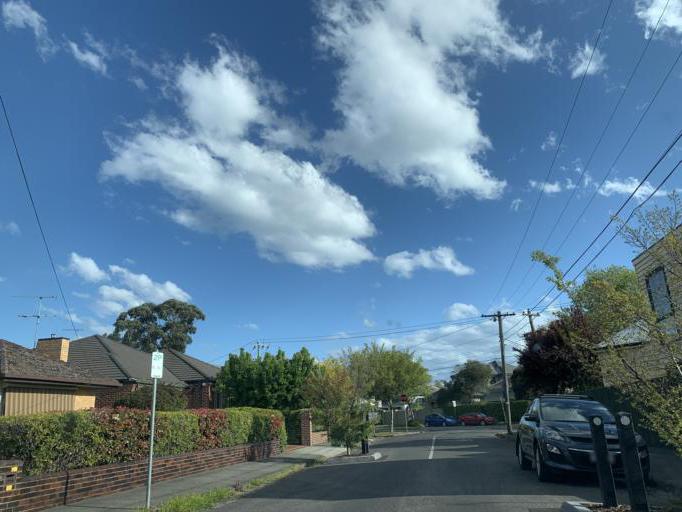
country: AU
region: Victoria
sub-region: Bayside
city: North Brighton
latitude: -37.9084
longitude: 145.0034
